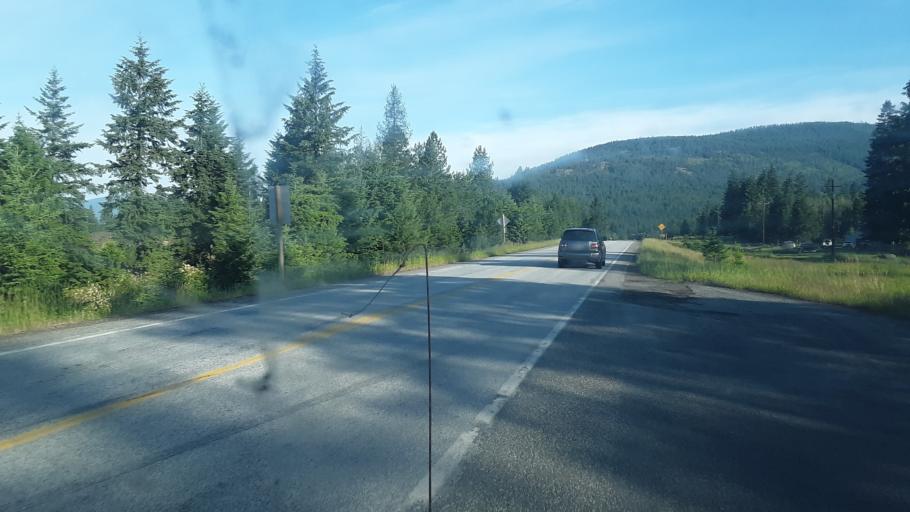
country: US
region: Idaho
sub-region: Boundary County
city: Bonners Ferry
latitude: 48.7238
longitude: -116.1710
